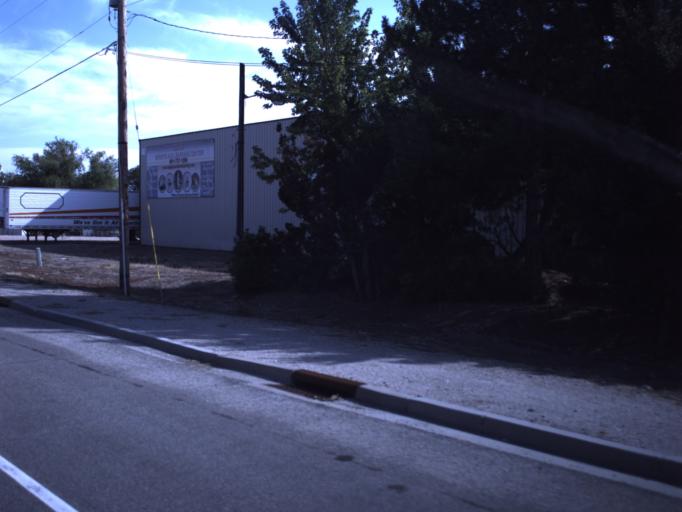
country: US
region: Utah
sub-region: Weber County
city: Pleasant View
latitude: 41.3040
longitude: -112.0031
